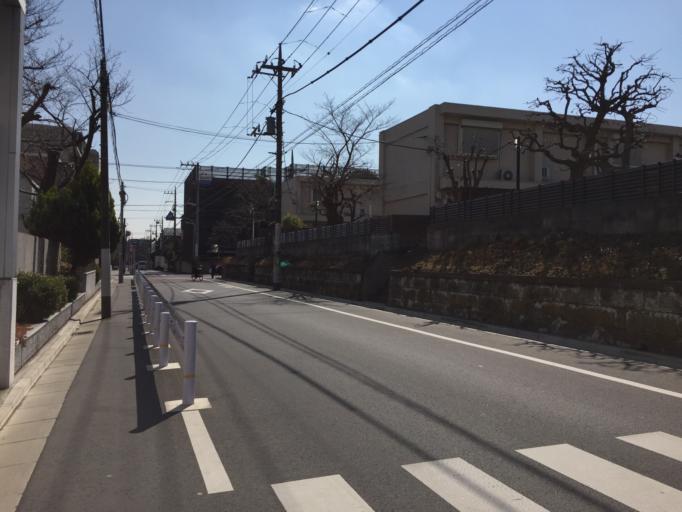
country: JP
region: Tokyo
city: Tokyo
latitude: 35.6231
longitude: 139.6475
